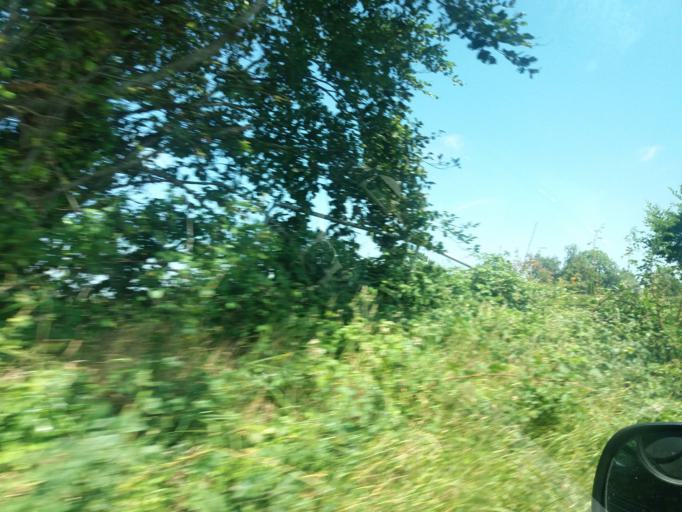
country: IE
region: Leinster
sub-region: Fingal County
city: Swords
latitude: 53.5143
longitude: -6.2382
